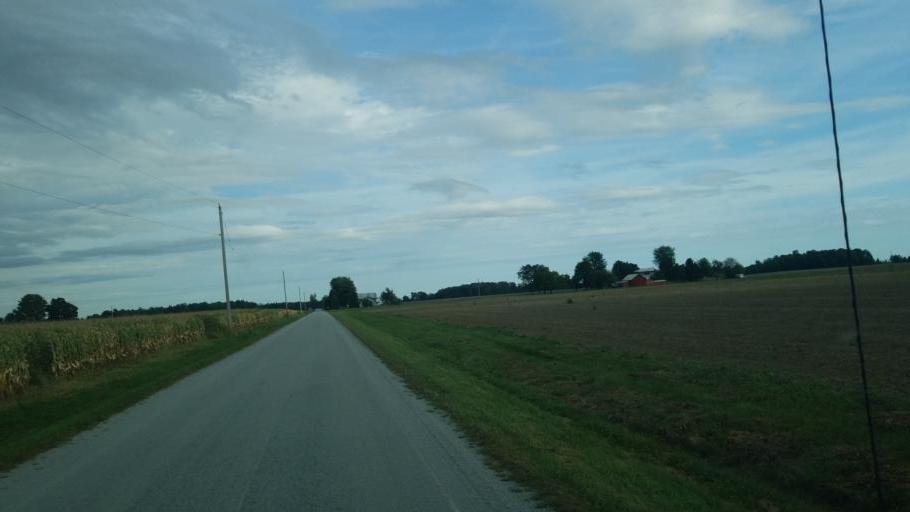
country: US
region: Ohio
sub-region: Hardin County
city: Forest
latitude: 40.8910
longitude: -83.4670
